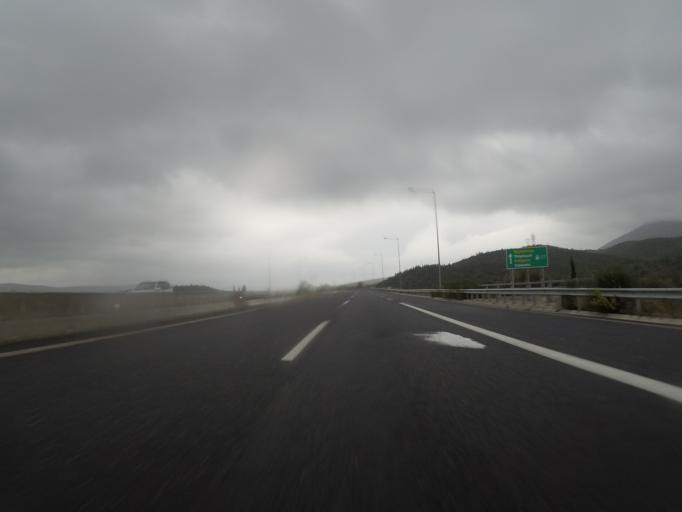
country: GR
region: Peloponnese
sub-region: Nomos Arkadias
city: Megalopoli
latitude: 37.3909
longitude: 22.2604
